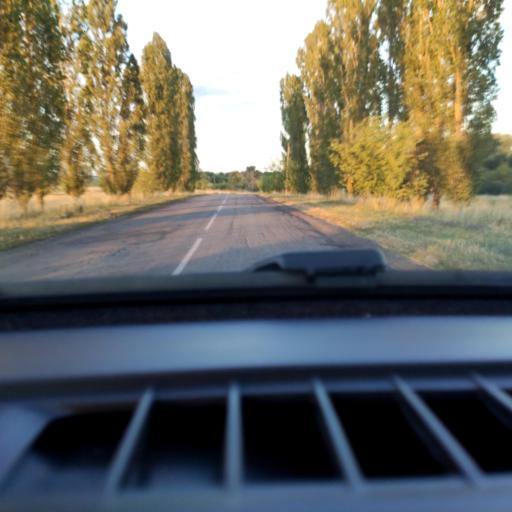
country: RU
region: Voronezj
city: Orlovo
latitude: 51.6160
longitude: 39.8032
